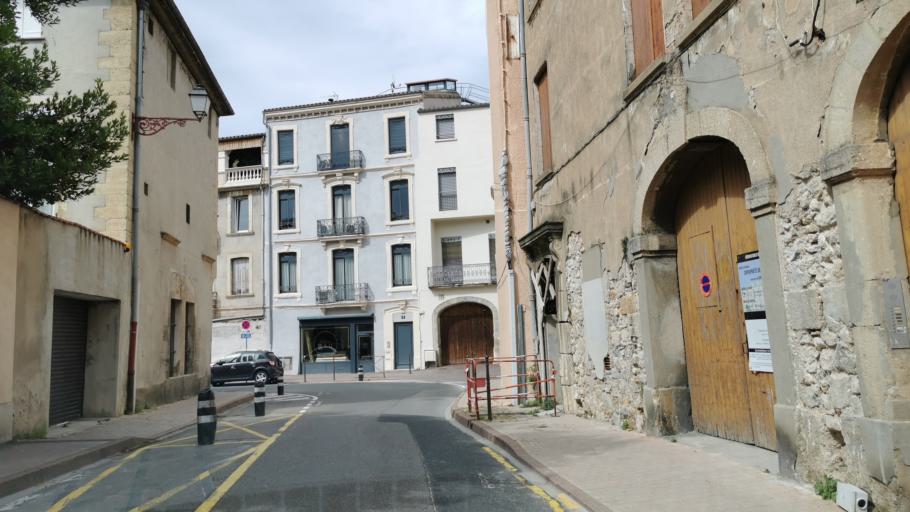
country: FR
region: Languedoc-Roussillon
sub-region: Departement de l'Aude
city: Narbonne
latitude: 43.1815
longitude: 3.0043
